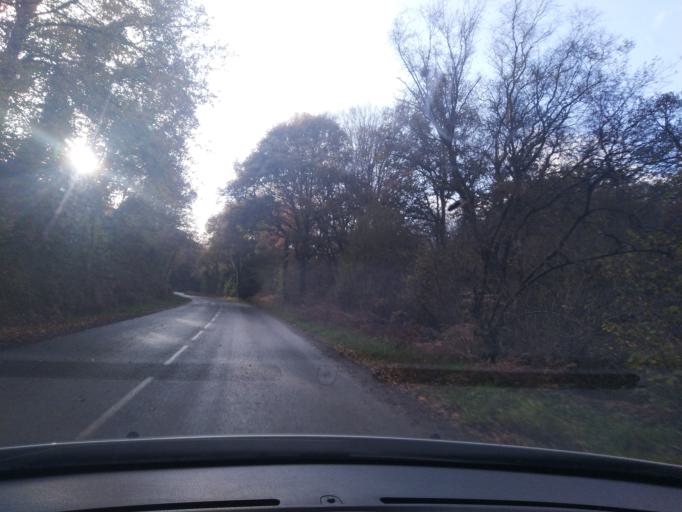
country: FR
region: Brittany
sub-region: Departement du Finistere
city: Plouigneau
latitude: 48.5710
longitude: -3.6647
